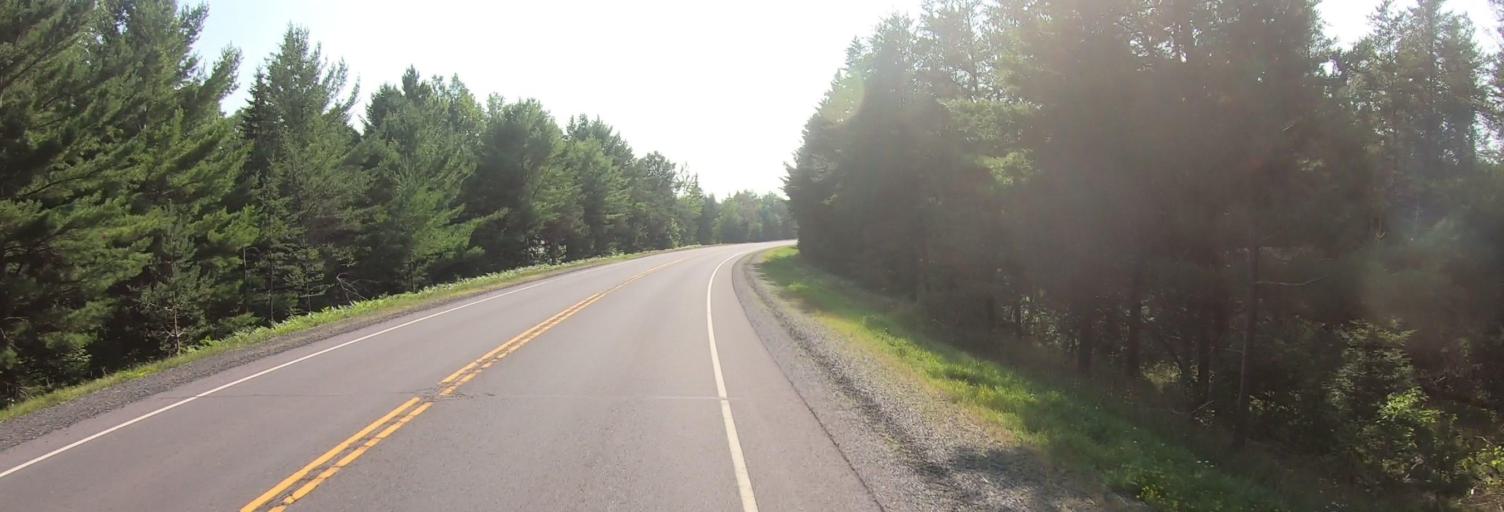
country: US
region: Wisconsin
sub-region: Iron County
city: Hurley
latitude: 46.3684
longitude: -90.4003
